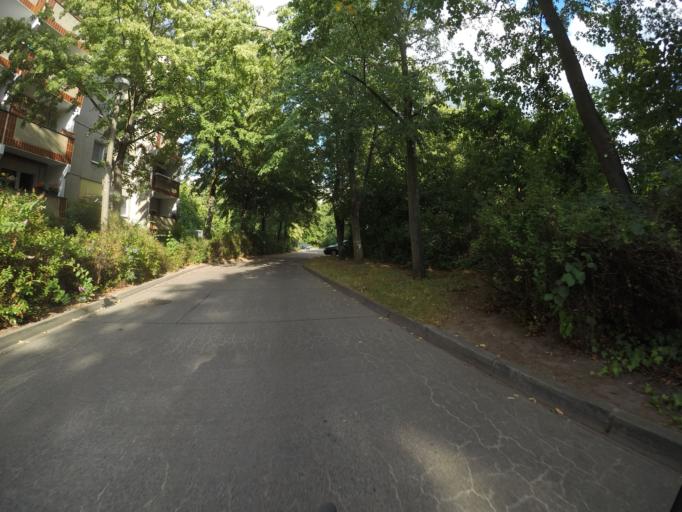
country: DE
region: Berlin
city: Hellersdorf
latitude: 52.5276
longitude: 13.6206
